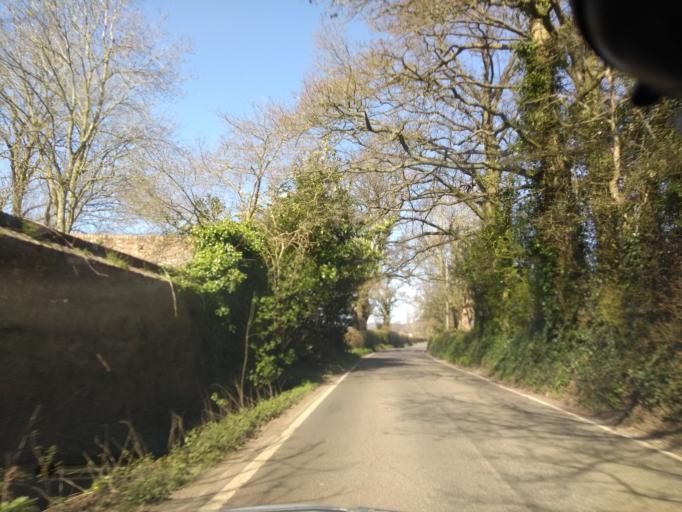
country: GB
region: England
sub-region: Somerset
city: Taunton
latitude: 51.0374
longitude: -3.1101
